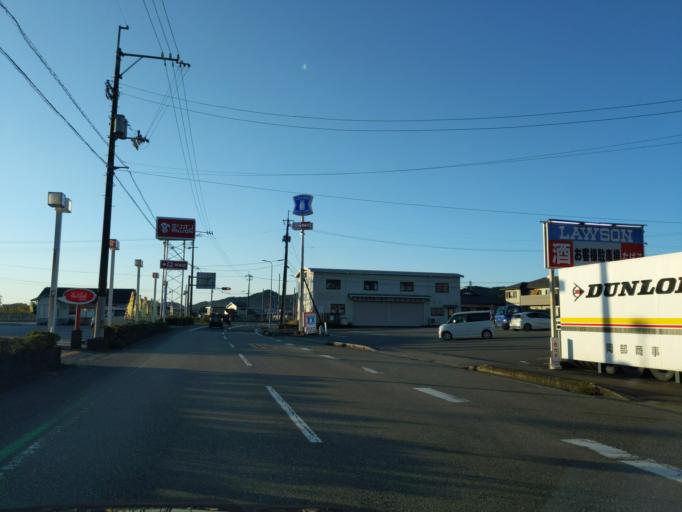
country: JP
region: Kochi
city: Muroto-misakicho
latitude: 33.6134
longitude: 134.3533
